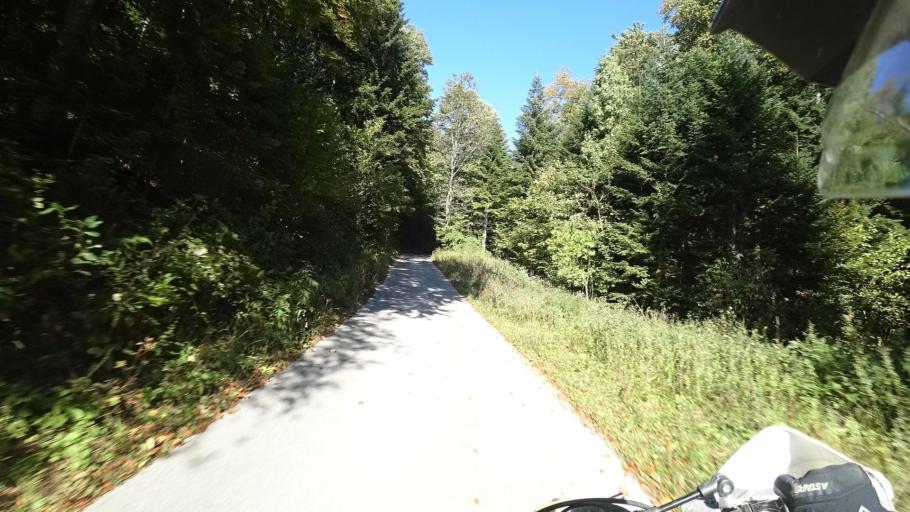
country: HR
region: Karlovacka
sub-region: Grad Ogulin
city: Ogulin
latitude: 45.2374
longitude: 15.1432
